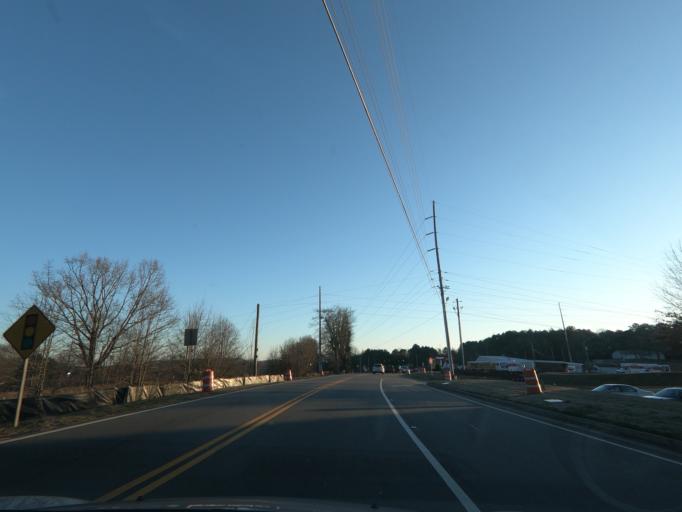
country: US
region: Georgia
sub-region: Forsyth County
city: Cumming
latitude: 34.3003
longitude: -84.1529
